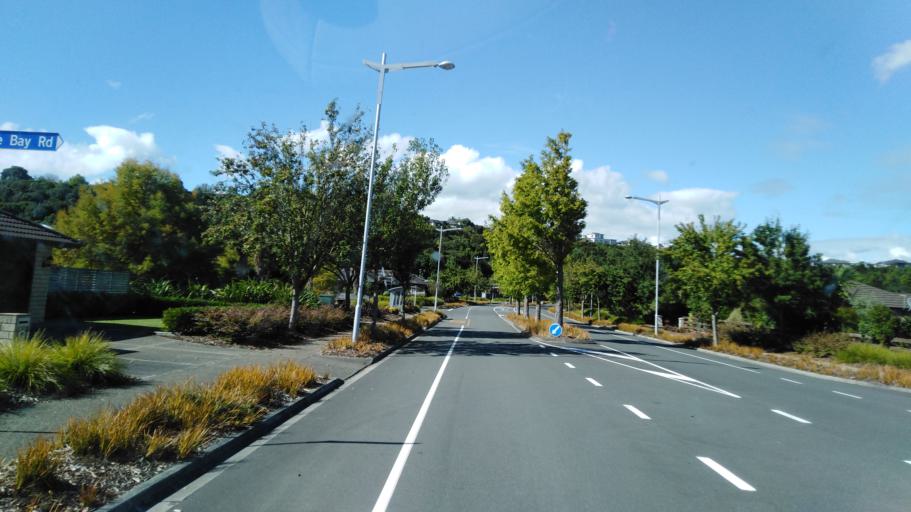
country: NZ
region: Bay of Plenty
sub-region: Tauranga City
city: Tauranga
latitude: -37.7466
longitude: 176.1093
